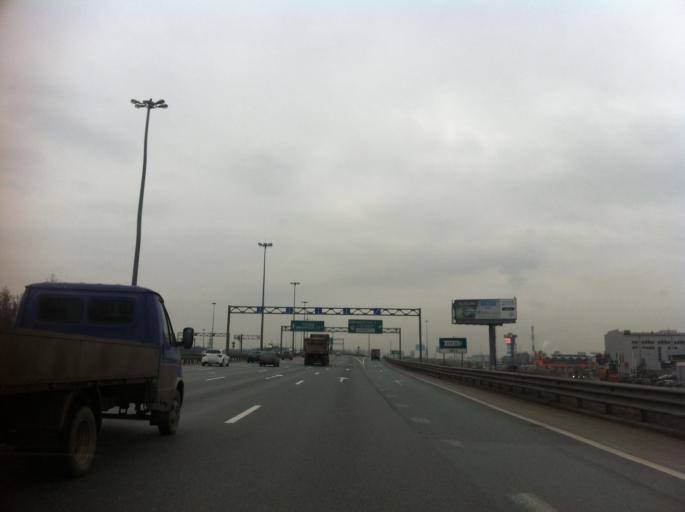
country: RU
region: Leningrad
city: Rybatskoye
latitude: 59.8988
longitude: 30.5253
